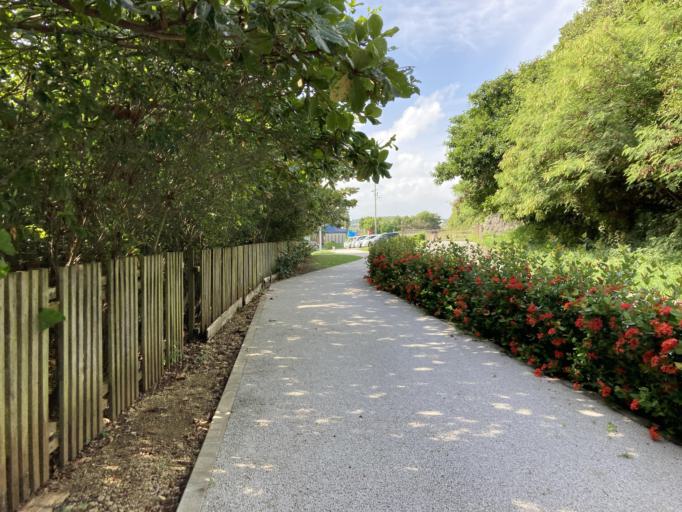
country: JP
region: Okinawa
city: Itoman
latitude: 26.0902
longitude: 127.7097
